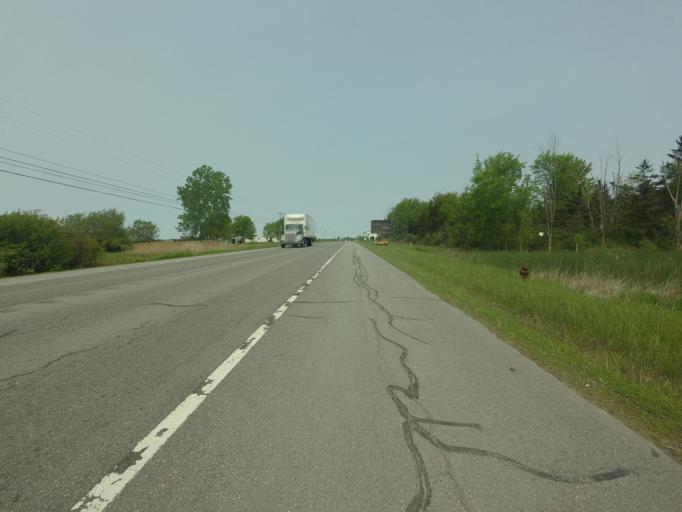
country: US
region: New York
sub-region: Jefferson County
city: Dexter
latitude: 44.0474
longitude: -76.0923
